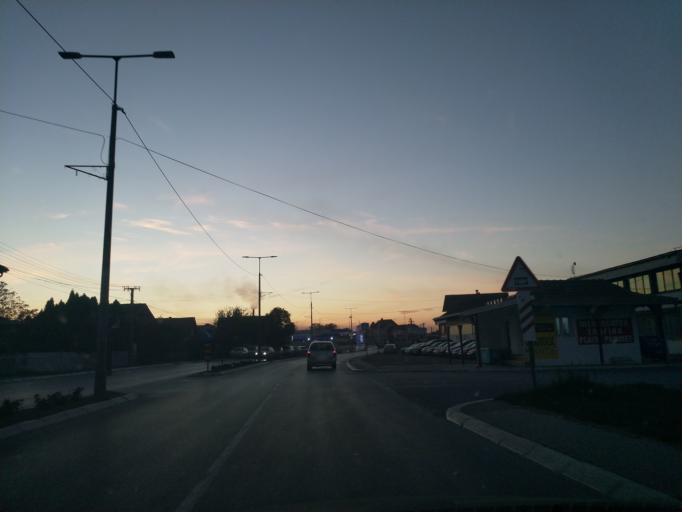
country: RS
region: Central Serbia
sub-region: Pomoravski Okrug
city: Svilajnac
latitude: 44.2327
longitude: 21.1885
